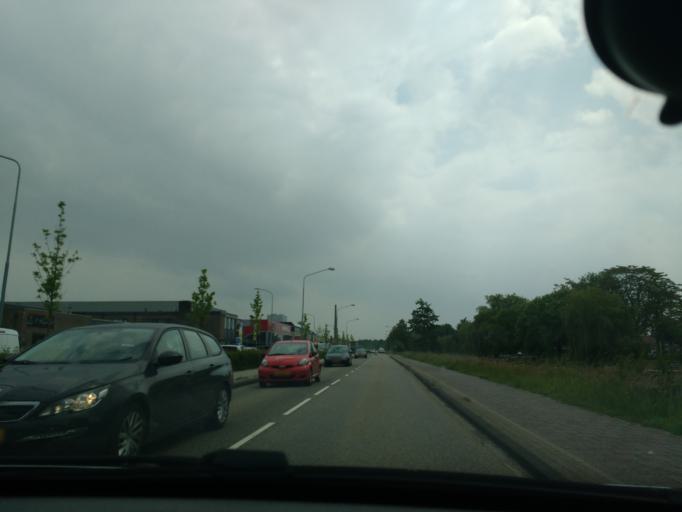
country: NL
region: North Holland
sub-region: Gemeente Naarden
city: Naarden
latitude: 52.3025
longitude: 5.1466
